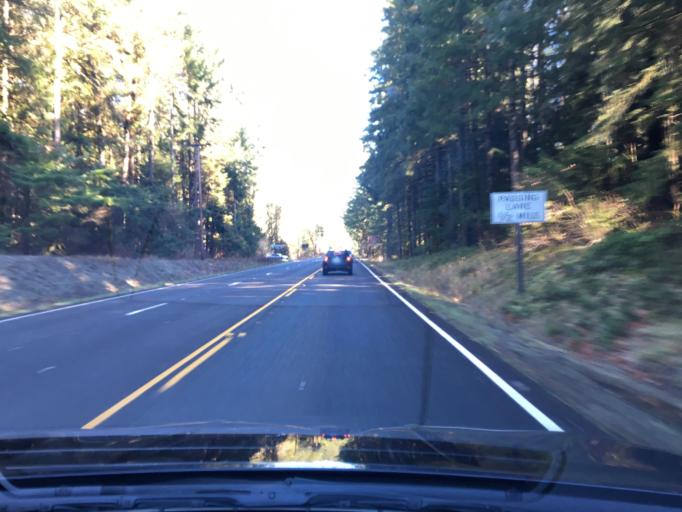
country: US
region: Oregon
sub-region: Douglas County
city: Glide
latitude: 43.2983
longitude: -122.9073
